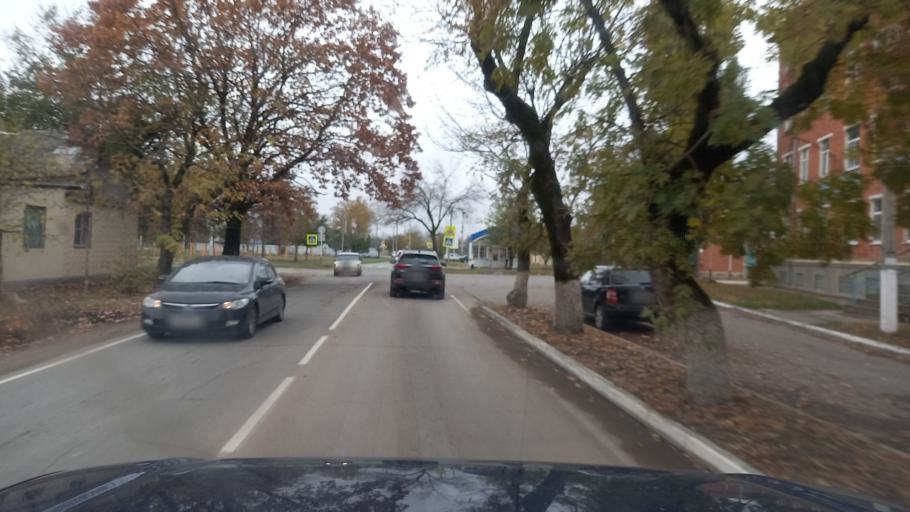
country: RU
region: Adygeya
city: Maykop
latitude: 44.6064
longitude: 40.0893
